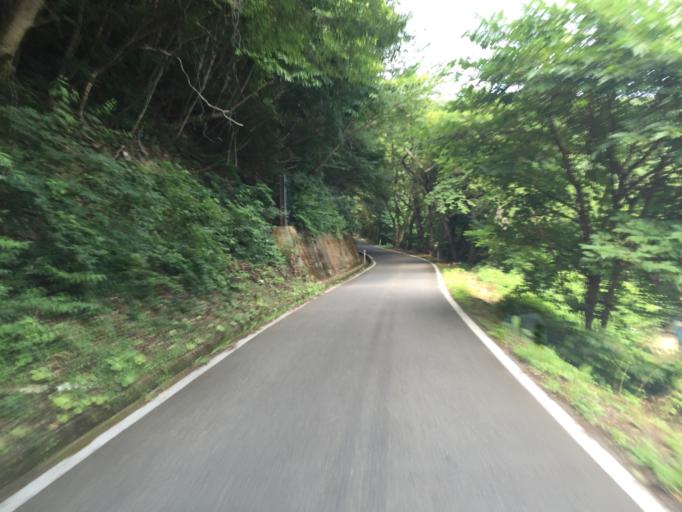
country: JP
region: Fukushima
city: Inawashiro
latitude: 37.4133
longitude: 140.1094
